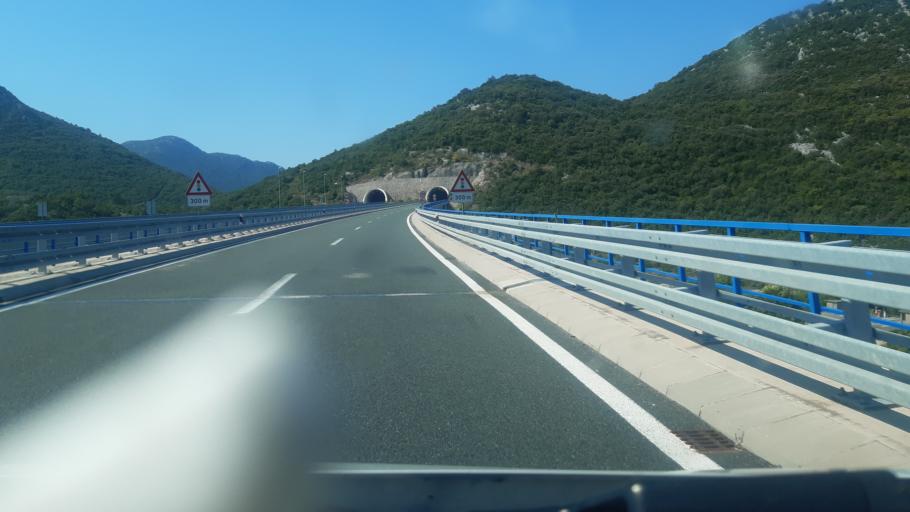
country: HR
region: Dubrovacko-Neretvanska
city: Komin
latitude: 43.1184
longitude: 17.4830
